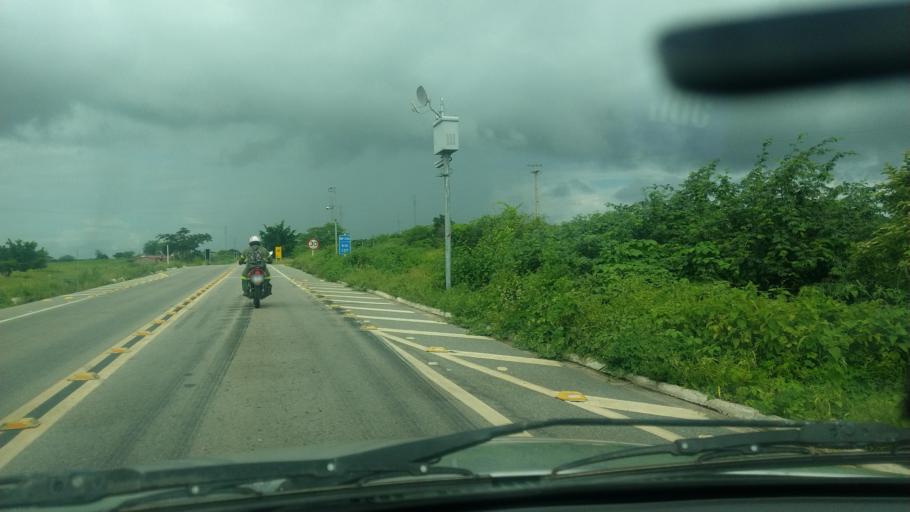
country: BR
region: Rio Grande do Norte
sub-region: Santa Cruz
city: Santa Cruz
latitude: -6.1927
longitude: -36.2139
